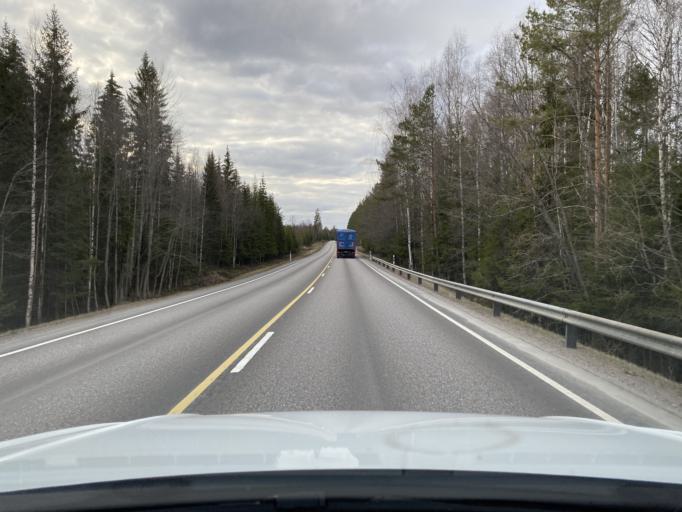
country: FI
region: Uusimaa
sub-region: Helsinki
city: Kaerkoelae
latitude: 60.8196
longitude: 24.0374
